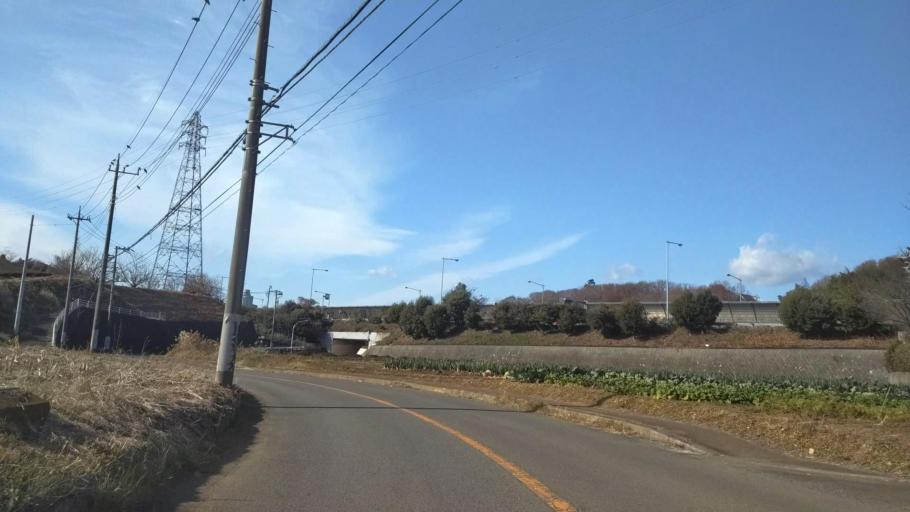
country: JP
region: Kanagawa
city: Hadano
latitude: 35.3499
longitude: 139.2297
